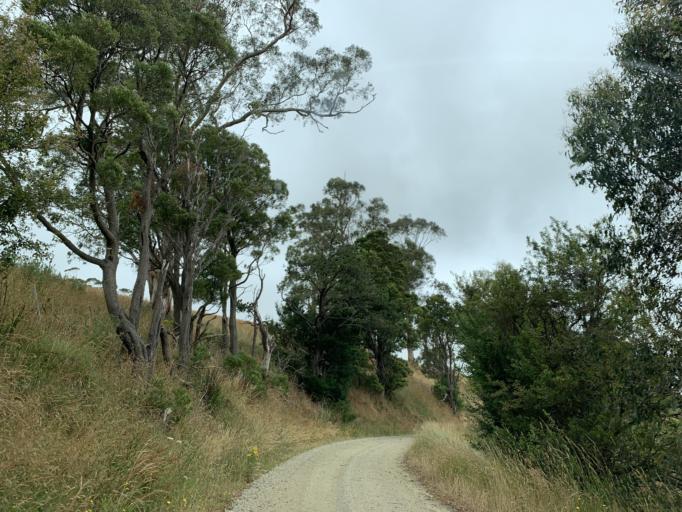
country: AU
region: Victoria
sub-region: Baw Baw
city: Warragul
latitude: -38.2984
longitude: 145.8875
